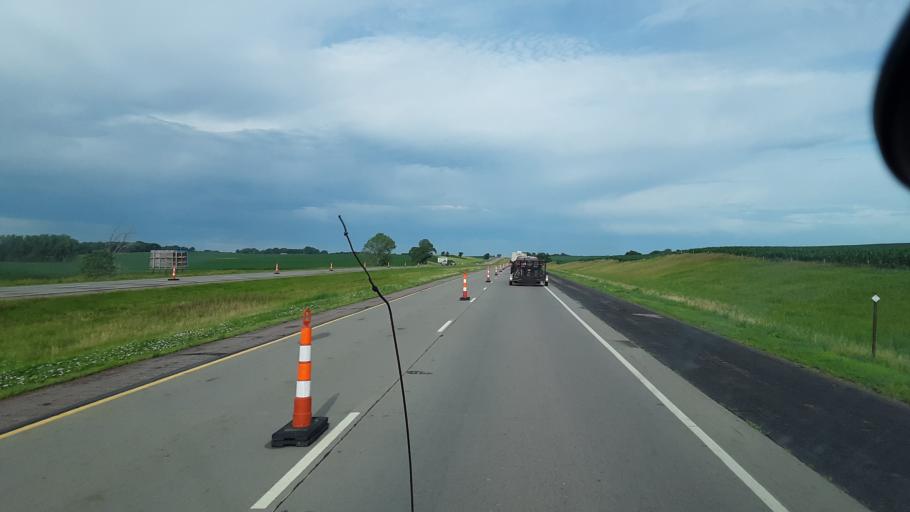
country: US
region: South Dakota
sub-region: Minnehaha County
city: Crooks
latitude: 43.6088
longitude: -96.8335
